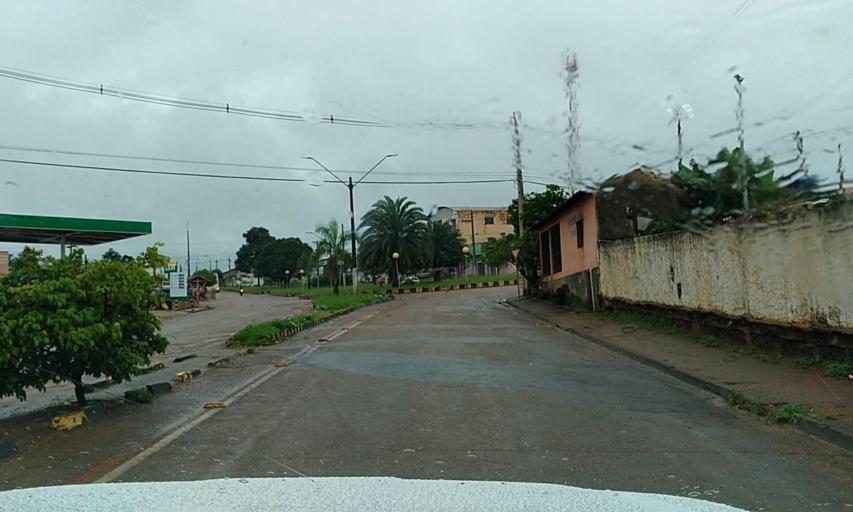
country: BR
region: Para
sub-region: Altamira
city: Altamira
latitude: -3.2126
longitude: -52.2319
